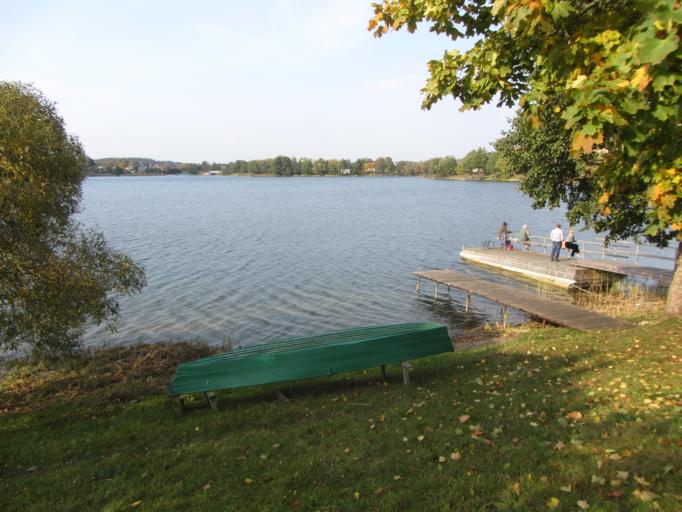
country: LT
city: Trakai
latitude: 54.6444
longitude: 24.9323
